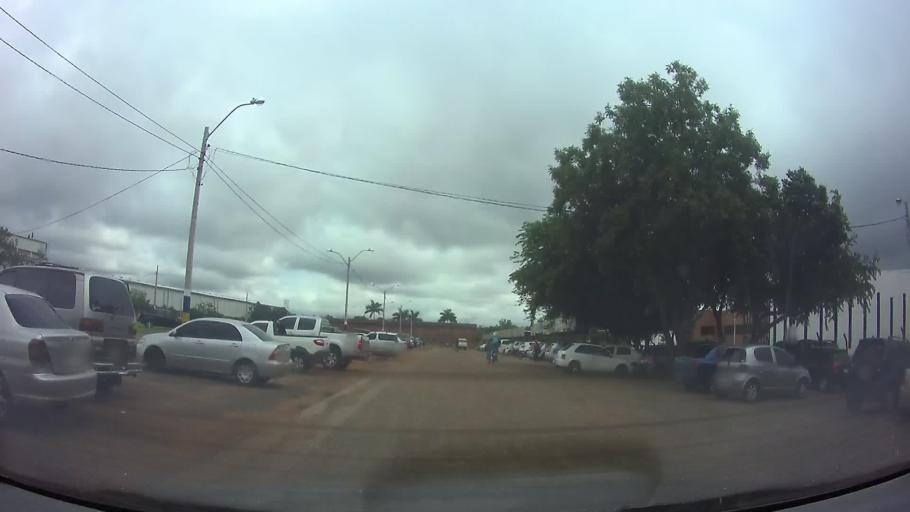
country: PY
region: Central
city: San Lorenzo
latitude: -25.2843
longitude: -57.4888
